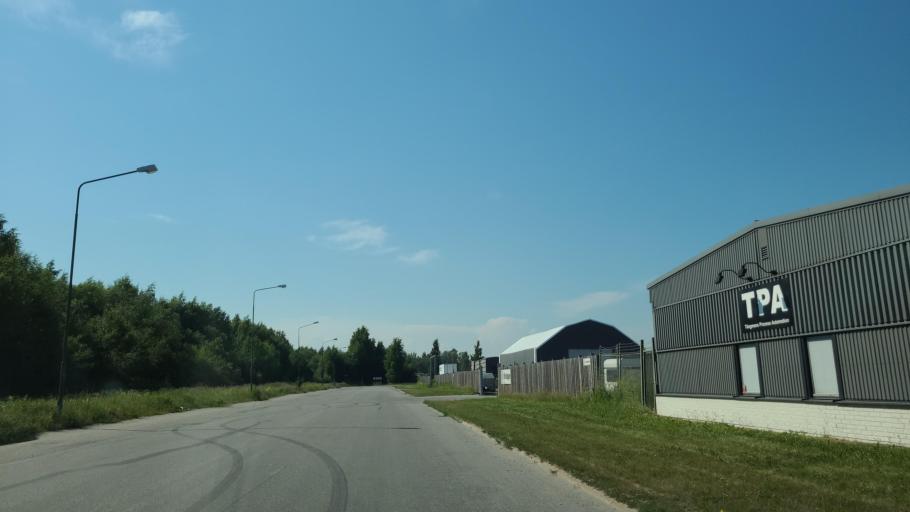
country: SE
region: Vaesterbotten
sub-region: Umea Kommun
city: Roback
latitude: 63.8443
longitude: 20.2147
